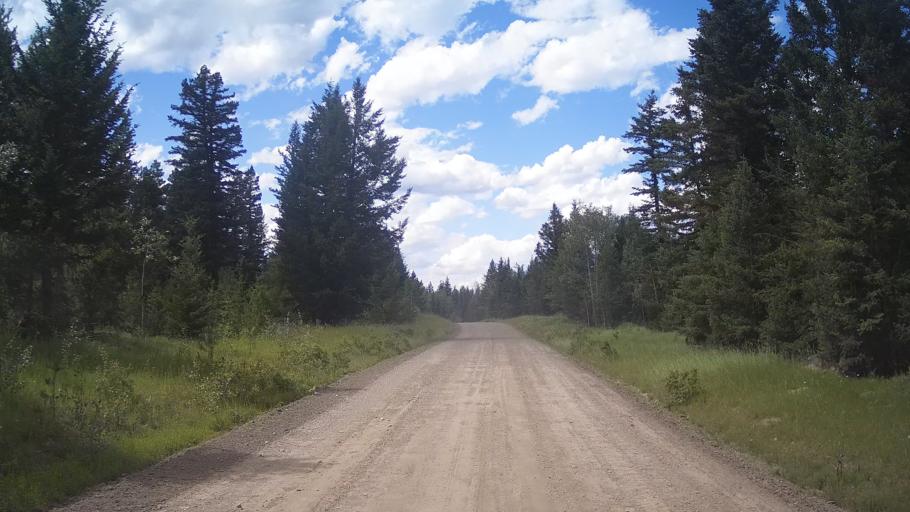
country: CA
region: British Columbia
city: Lillooet
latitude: 51.3226
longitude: -121.8676
